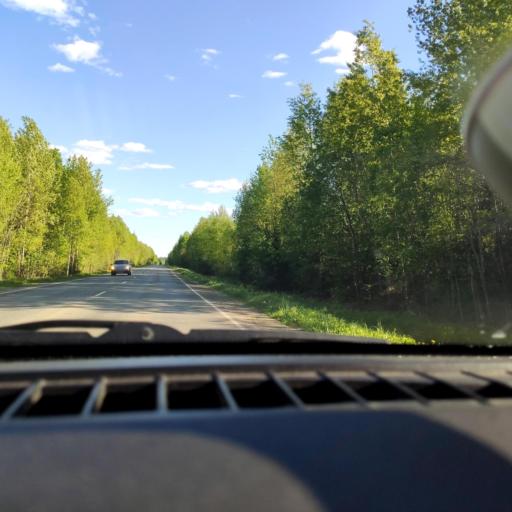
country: RU
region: Perm
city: Polazna
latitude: 58.2887
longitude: 56.1634
